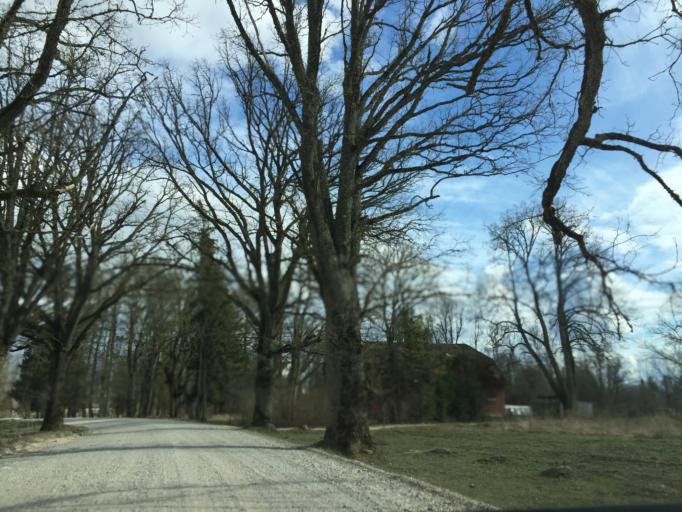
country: LV
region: Burtnieki
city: Matisi
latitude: 57.6153
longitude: 25.0774
